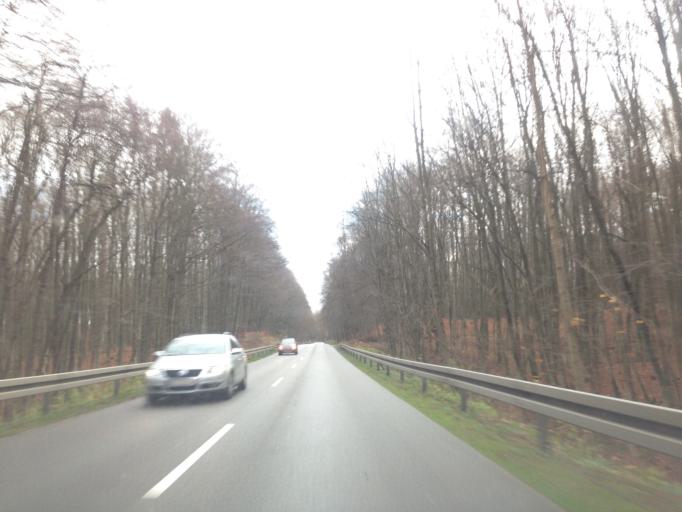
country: PL
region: Pomeranian Voivodeship
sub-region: Powiat gdanski
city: Kolbudy
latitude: 54.2540
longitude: 18.4111
